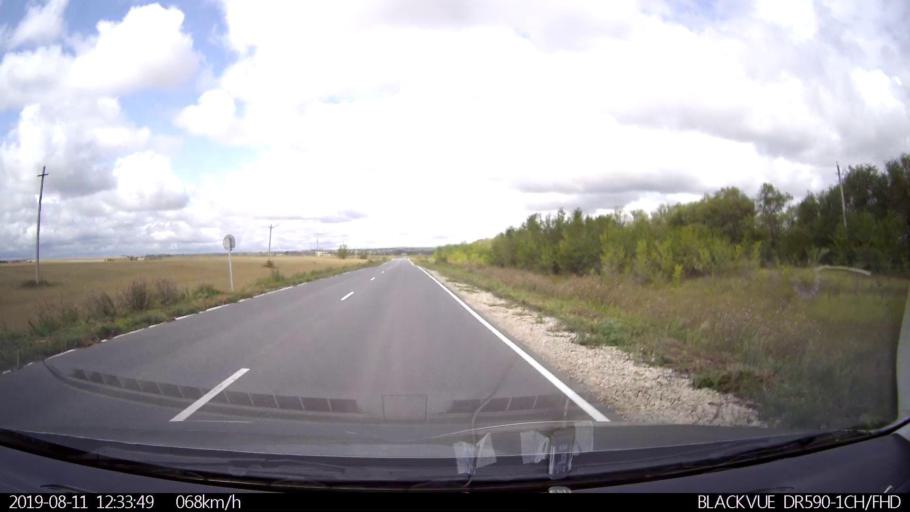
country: RU
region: Ulyanovsk
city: Ignatovka
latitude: 53.8122
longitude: 47.8512
